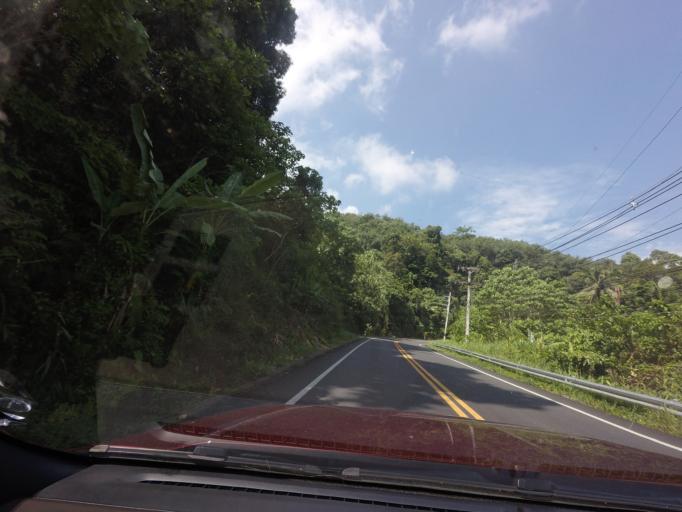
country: TH
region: Yala
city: Betong
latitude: 5.9112
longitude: 101.1544
